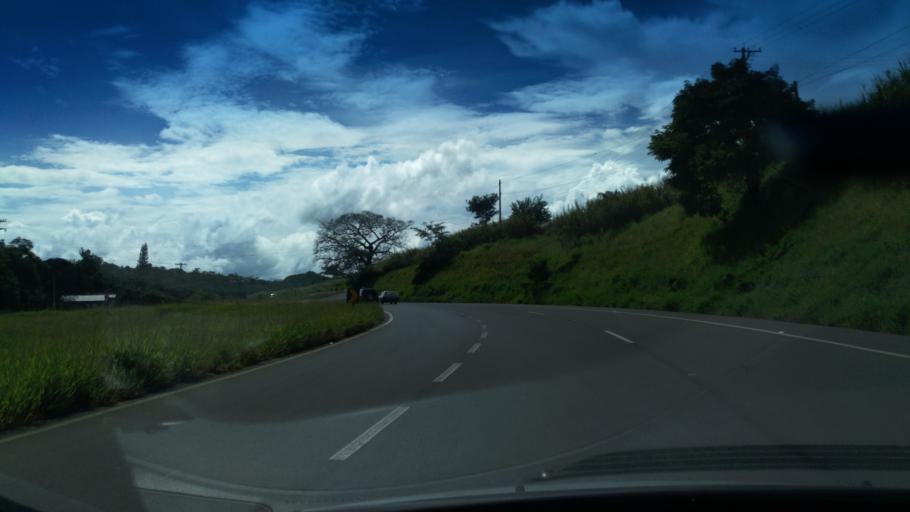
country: BR
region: Sao Paulo
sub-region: Santo Antonio Do Jardim
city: Espirito Santo do Pinhal
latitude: -22.1657
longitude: -46.7373
